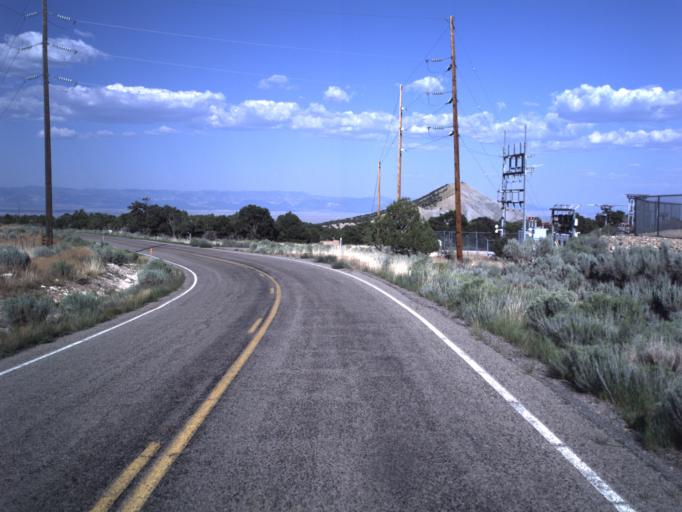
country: US
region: Utah
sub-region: Emery County
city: Huntington
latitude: 39.4841
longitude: -110.9660
